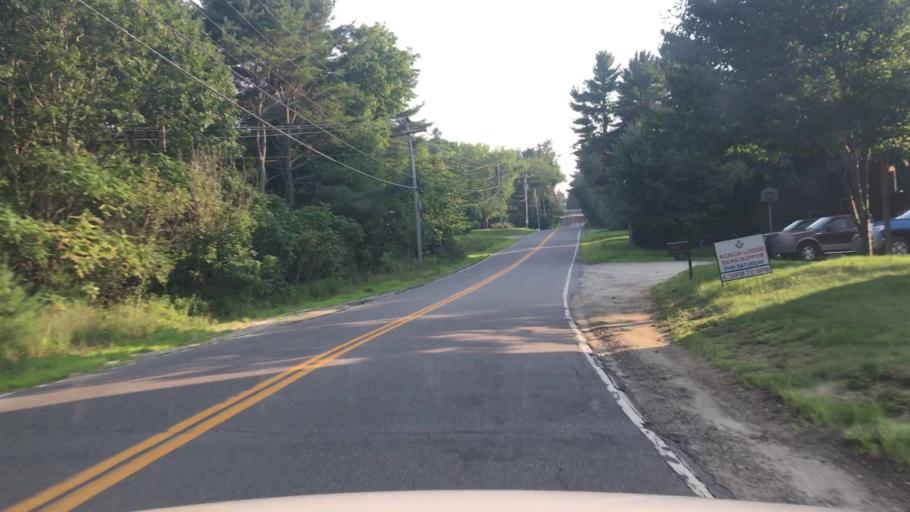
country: US
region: Maine
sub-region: Androscoggin County
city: Lisbon Falls
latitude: 43.9880
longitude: -70.0531
